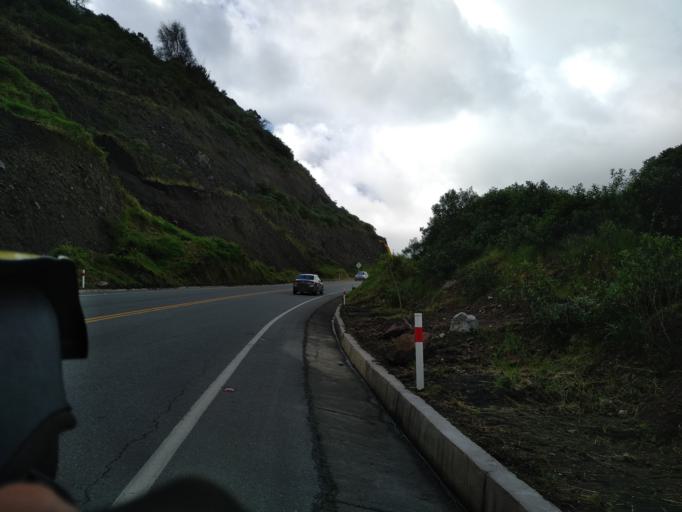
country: EC
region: Tungurahua
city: Banos
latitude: -1.4773
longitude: -78.5182
